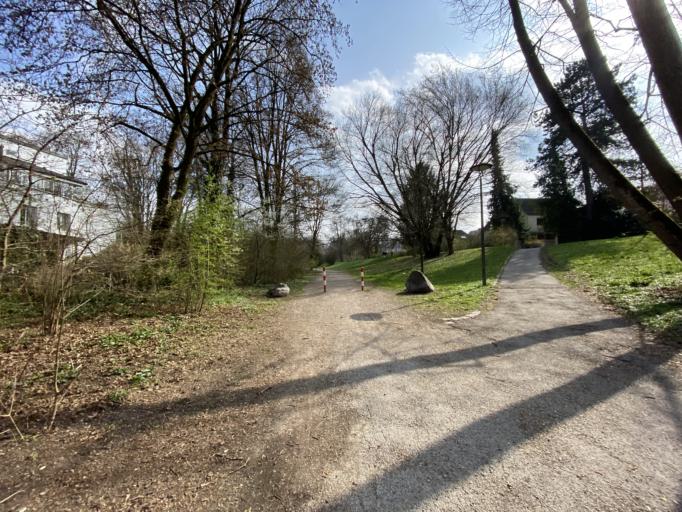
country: DE
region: Bavaria
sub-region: Upper Bavaria
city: Bogenhausen
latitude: 48.1797
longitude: 11.6093
